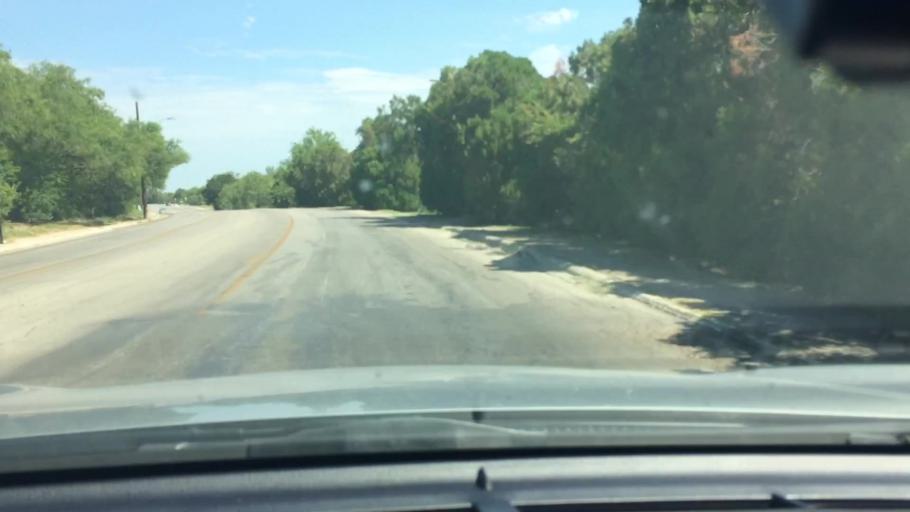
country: US
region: Texas
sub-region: Bexar County
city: San Antonio
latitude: 29.3816
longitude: -98.4306
